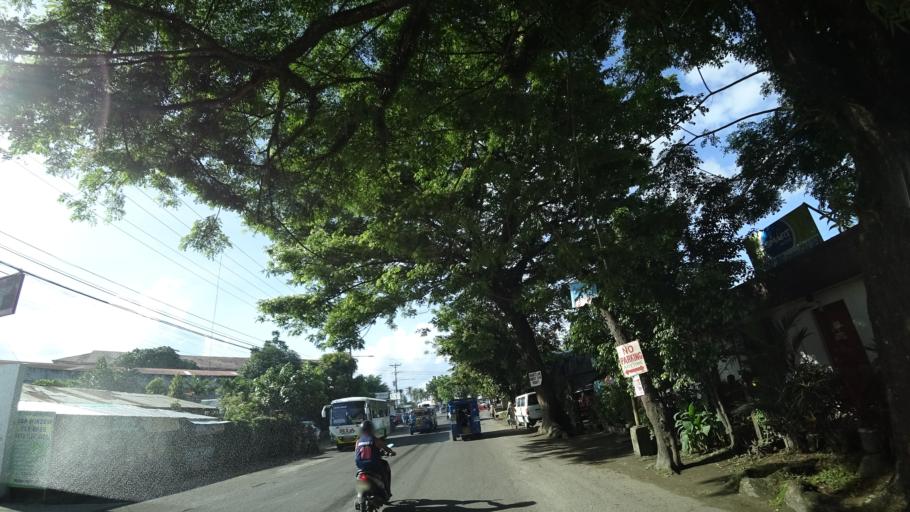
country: PH
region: Eastern Visayas
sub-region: Province of Leyte
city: Panalanoy
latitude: 11.2184
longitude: 124.9937
